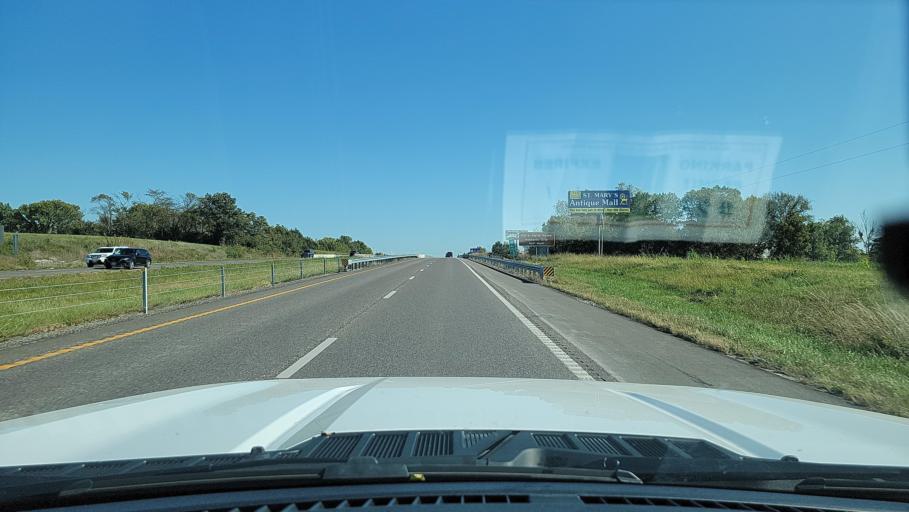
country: US
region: Missouri
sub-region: Sainte Genevieve County
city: Sainte Genevieve
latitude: 37.9422
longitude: -90.1336
